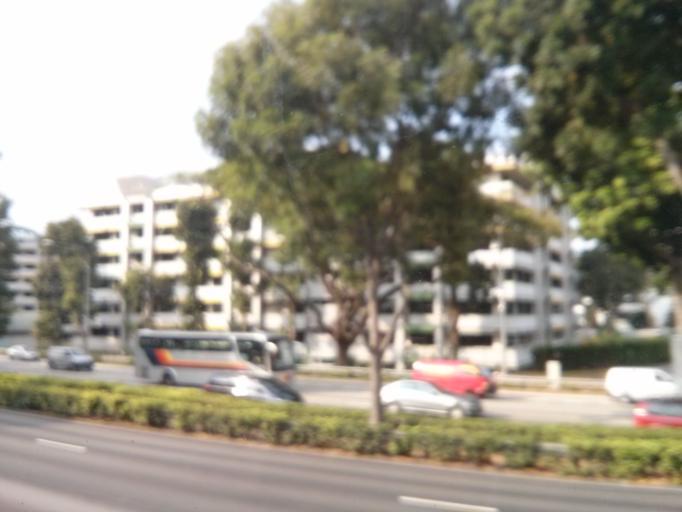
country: SG
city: Singapore
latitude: 1.2923
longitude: 103.7880
